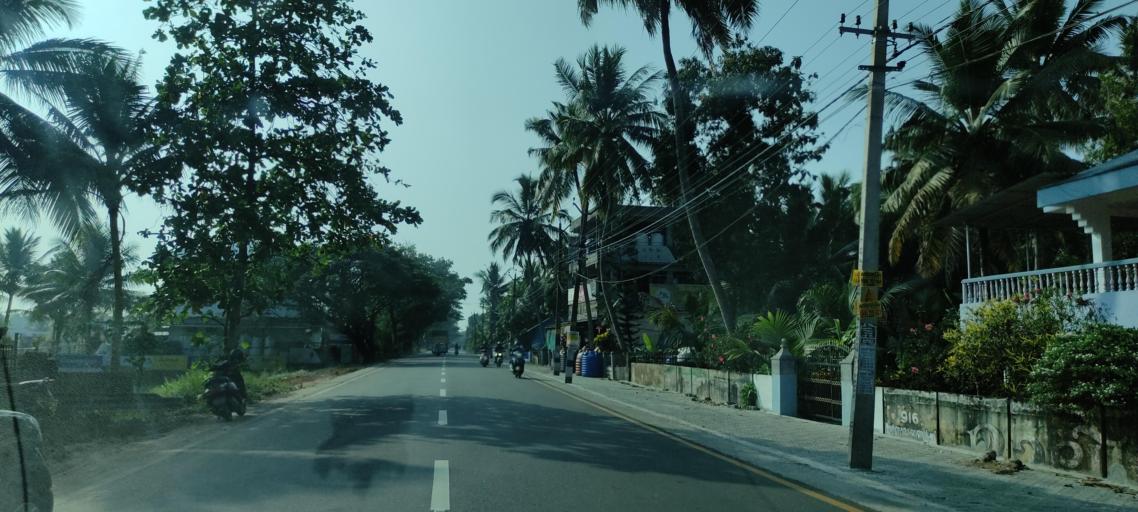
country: IN
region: Kerala
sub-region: Kottayam
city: Changanacheri
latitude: 9.3618
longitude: 76.4644
